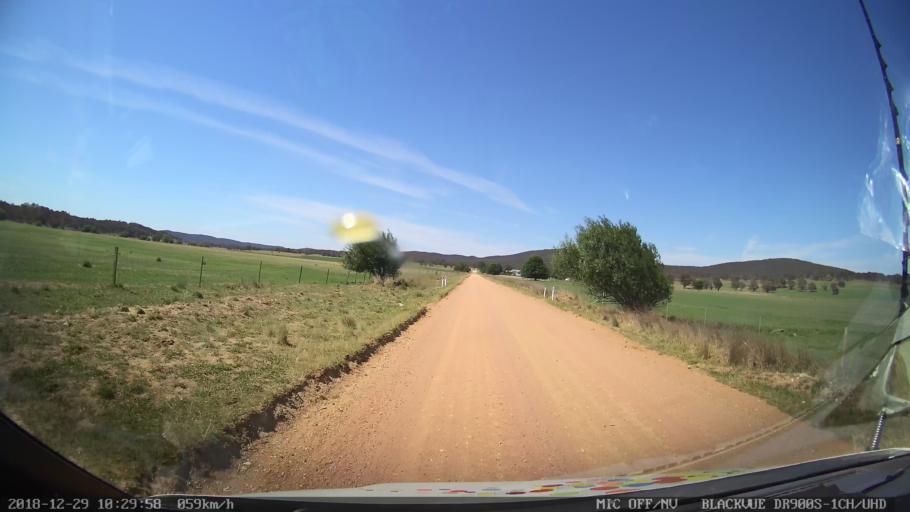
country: AU
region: New South Wales
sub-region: Yass Valley
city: Gundaroo
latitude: -34.9562
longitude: 149.4555
